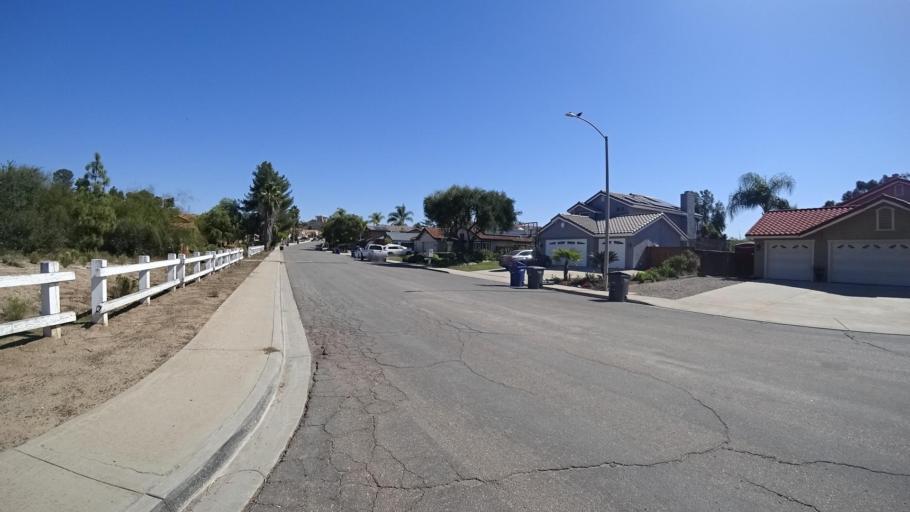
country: US
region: California
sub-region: San Diego County
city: Rancho San Diego
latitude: 32.7581
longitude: -116.9428
